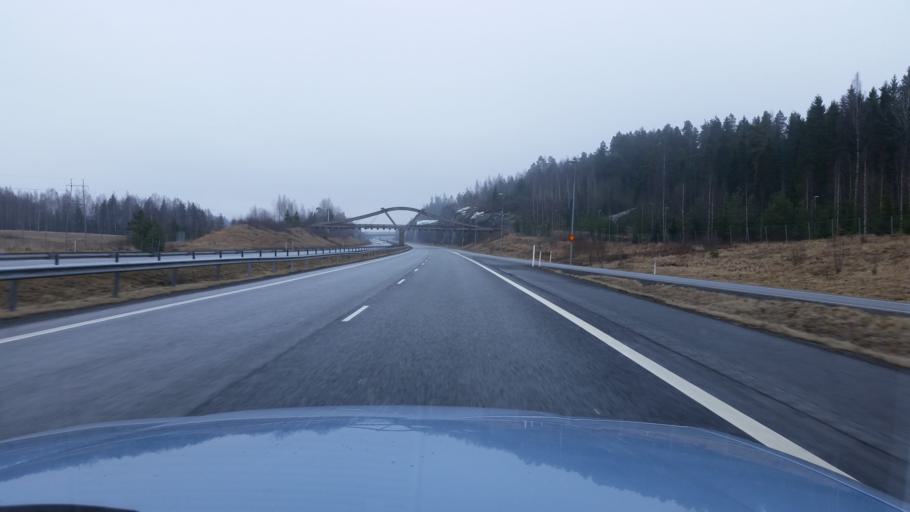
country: FI
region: Pirkanmaa
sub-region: Etelae-Pirkanmaa
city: Akaa
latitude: 61.1811
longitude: 23.8933
